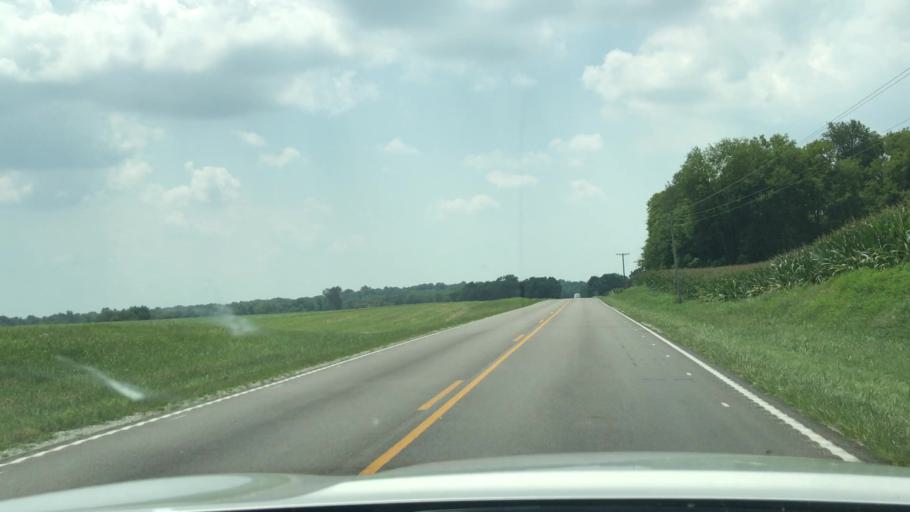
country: US
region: Kentucky
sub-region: Todd County
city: Guthrie
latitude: 36.7183
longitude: -87.0937
